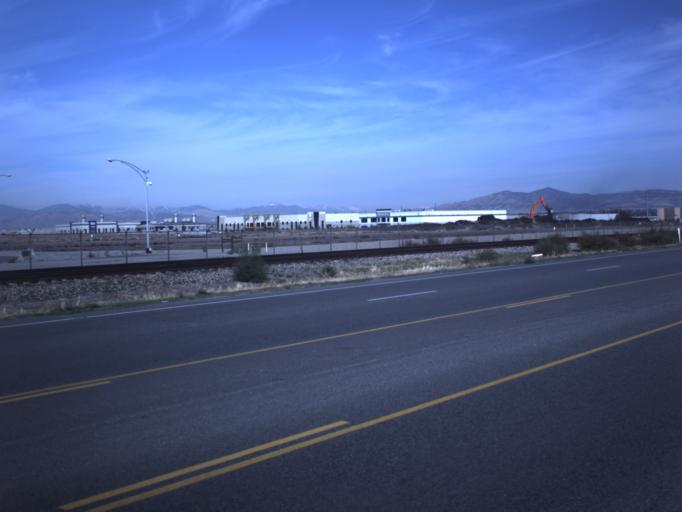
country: US
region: Utah
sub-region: Utah County
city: Lindon
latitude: 40.3228
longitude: -111.7366
